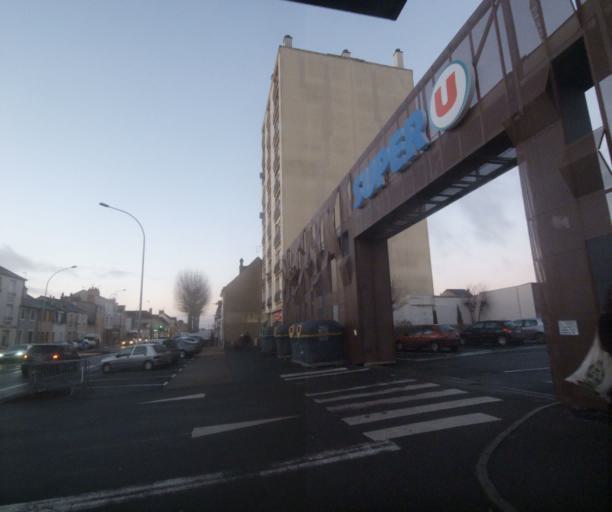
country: FR
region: Pays de la Loire
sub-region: Departement de la Sarthe
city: Le Mans
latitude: 48.0025
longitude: 0.1850
